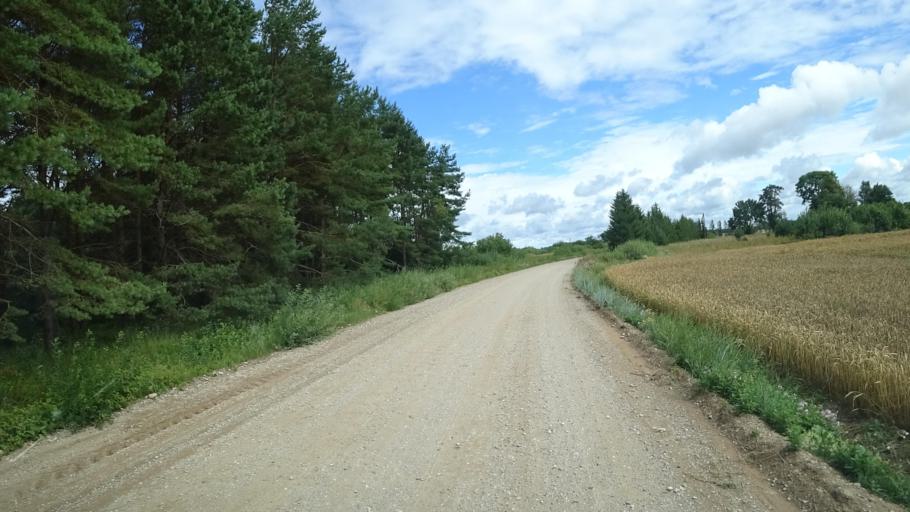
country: LV
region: Liepaja
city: Vec-Liepaja
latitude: 56.6482
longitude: 21.0449
